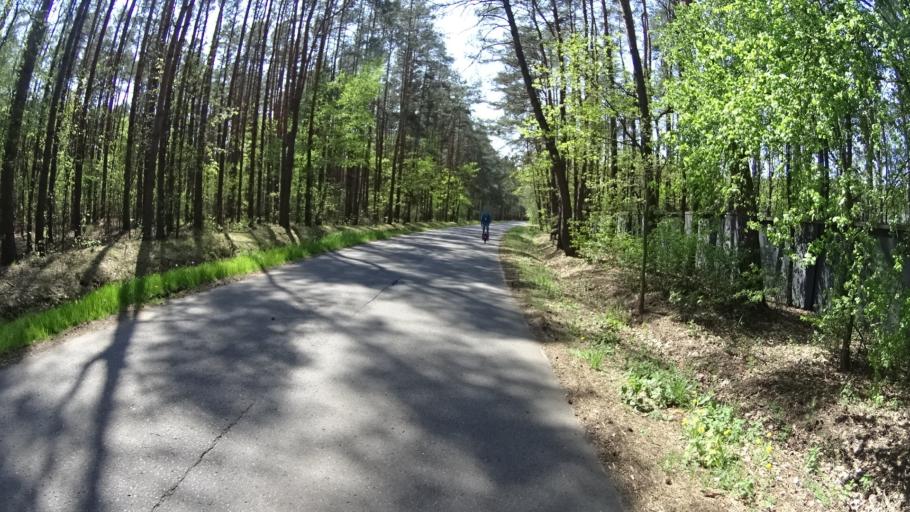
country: PL
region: Masovian Voivodeship
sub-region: Powiat warszawski zachodni
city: Truskaw
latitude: 52.2801
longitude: 20.7250
